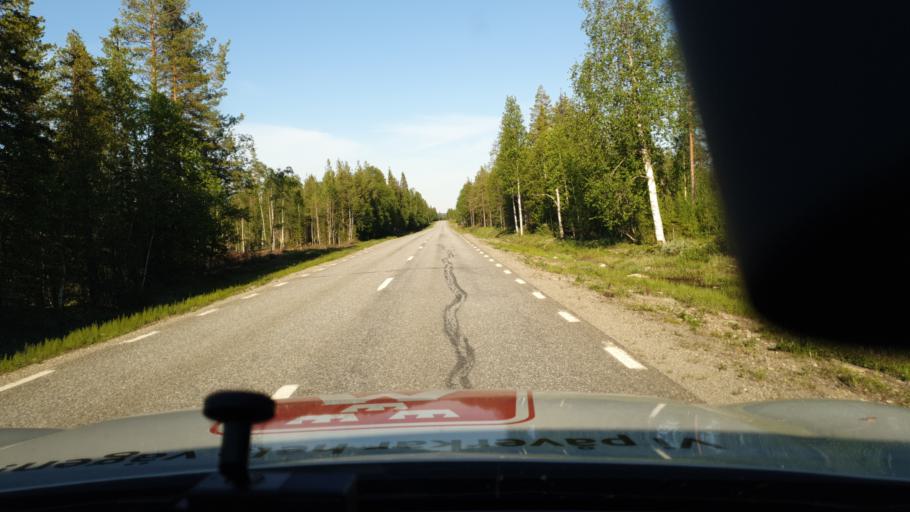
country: SE
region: Vaesterbotten
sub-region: Lycksele Kommun
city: Soderfors
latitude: 64.6337
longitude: 17.9436
